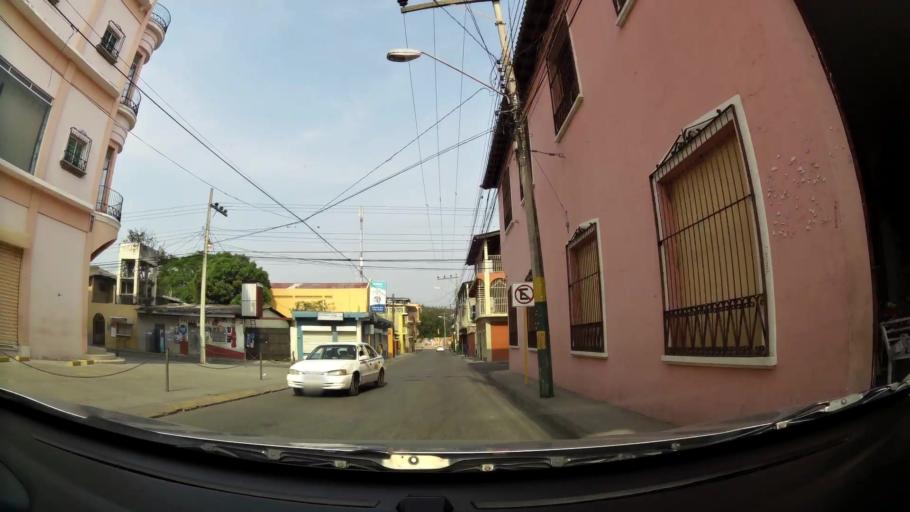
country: HN
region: Comayagua
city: Comayagua
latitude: 14.4561
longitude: -87.6428
